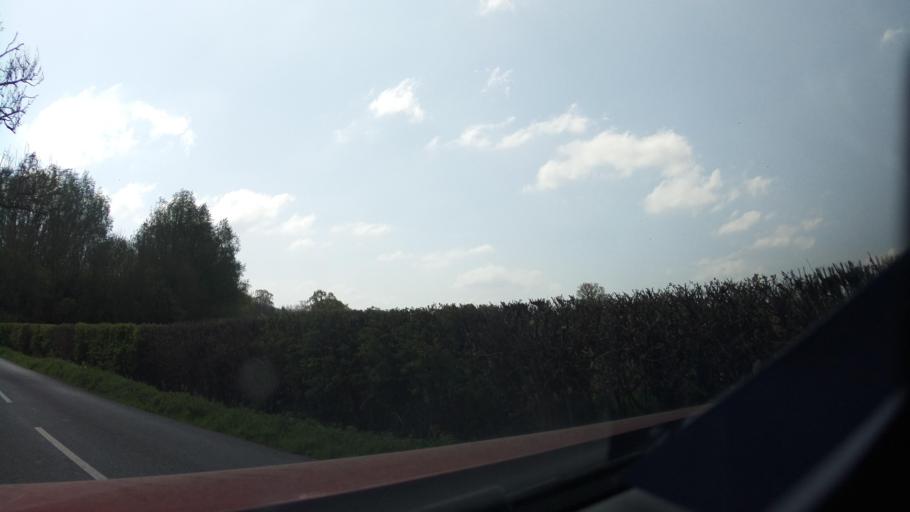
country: GB
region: England
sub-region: Gloucestershire
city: Wotton-under-Edge
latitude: 51.6096
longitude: -2.3436
